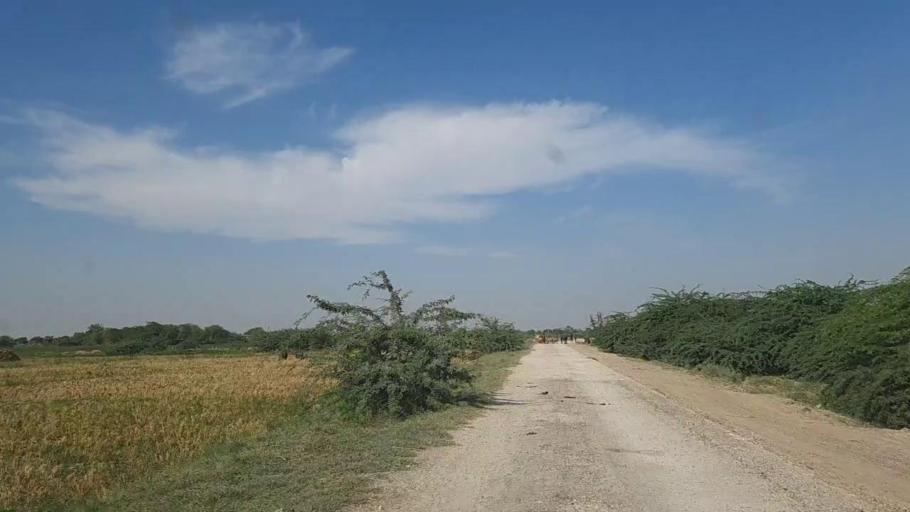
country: PK
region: Sindh
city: Bulri
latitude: 24.8367
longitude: 68.2736
